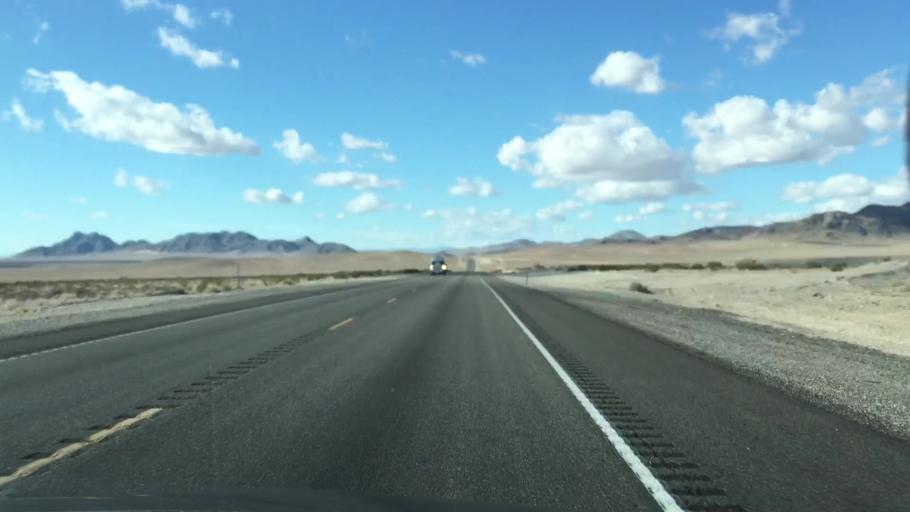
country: US
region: Nevada
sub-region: Nye County
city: Pahrump
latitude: 36.6028
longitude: -116.2528
